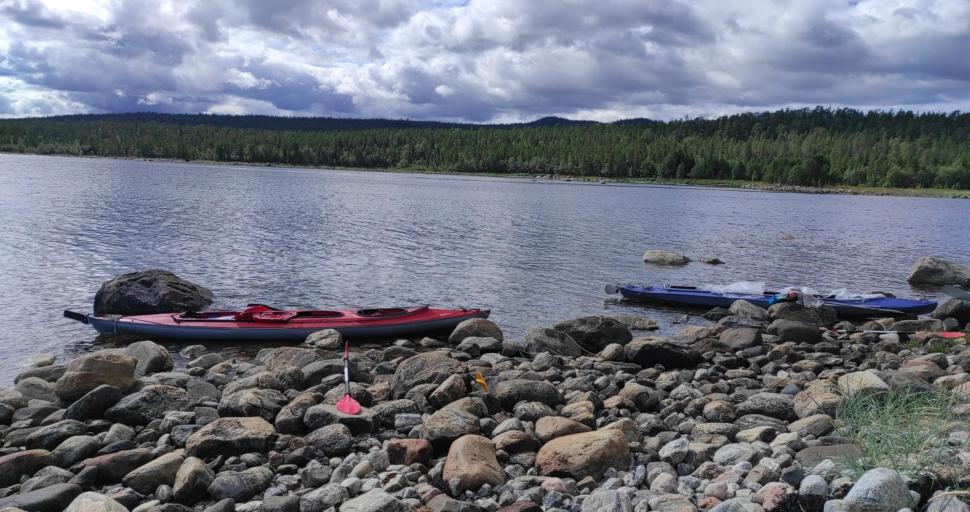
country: RU
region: Murmansk
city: Zelenoborskiy
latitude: 66.8583
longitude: 32.5796
